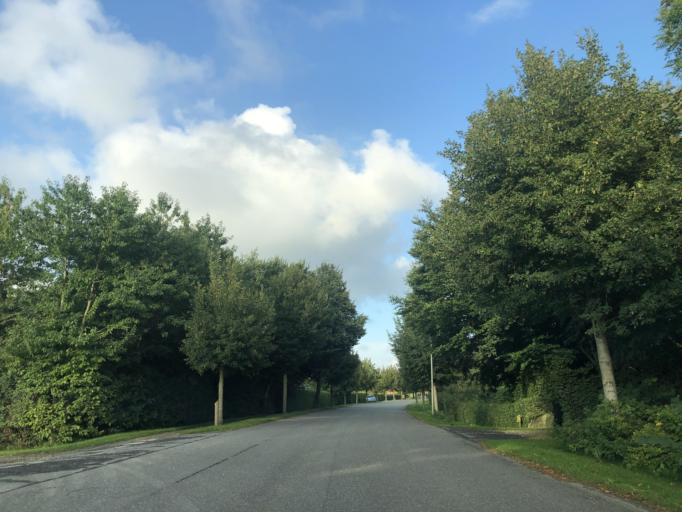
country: DK
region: North Denmark
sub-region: Vesthimmerland Kommune
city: Aars
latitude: 56.7852
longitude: 9.5887
